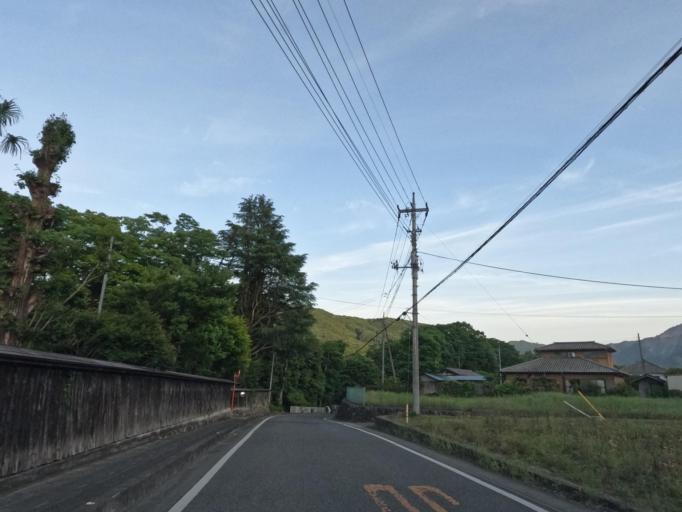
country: JP
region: Saitama
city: Chichibu
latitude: 36.0140
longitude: 139.1090
